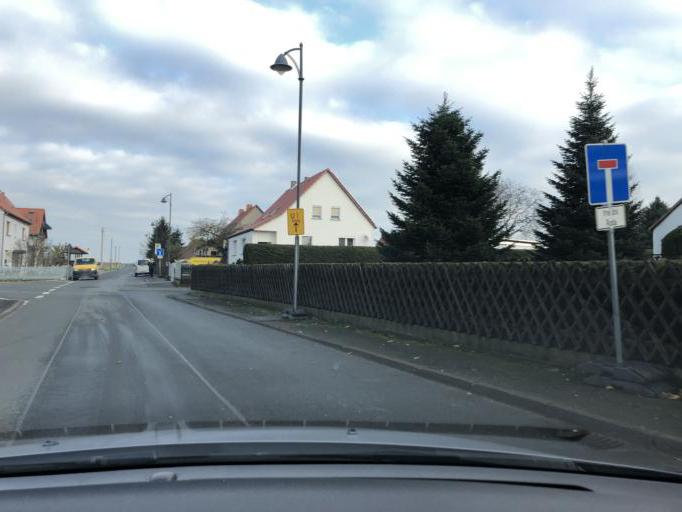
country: DE
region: Saxony
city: Nerchau
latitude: 51.2759
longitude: 12.8335
